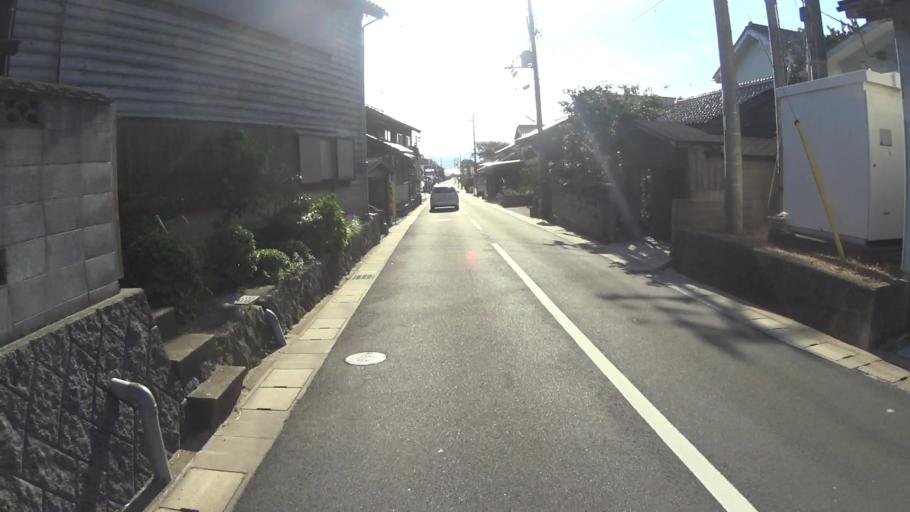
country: JP
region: Hyogo
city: Toyooka
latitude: 35.6628
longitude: 134.9682
